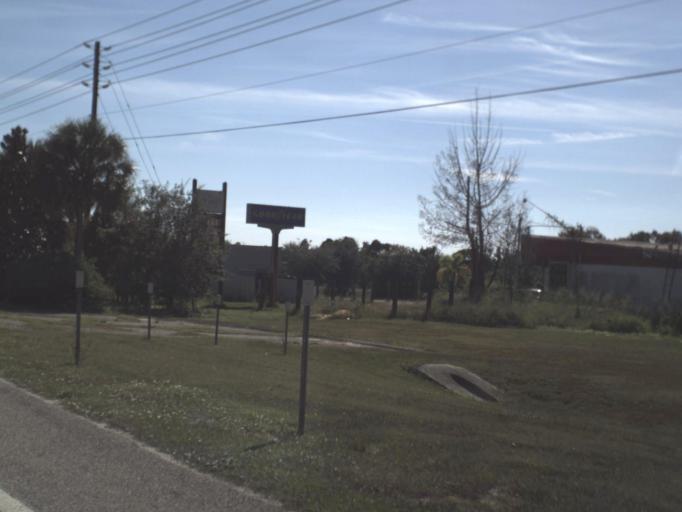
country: US
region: Florida
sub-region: Highlands County
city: Lake Placid
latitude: 27.2876
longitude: -81.3581
